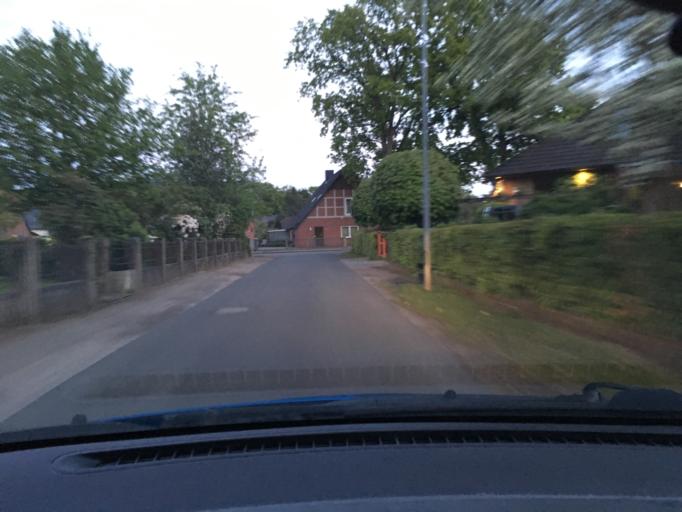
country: DE
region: Lower Saxony
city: Winsen
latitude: 53.3332
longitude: 10.2007
